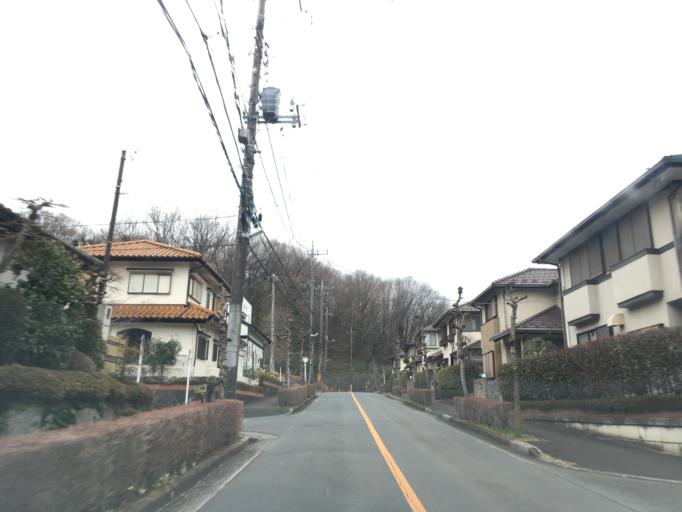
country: JP
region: Tokyo
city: Higashimurayama-shi
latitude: 35.7740
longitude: 139.4598
